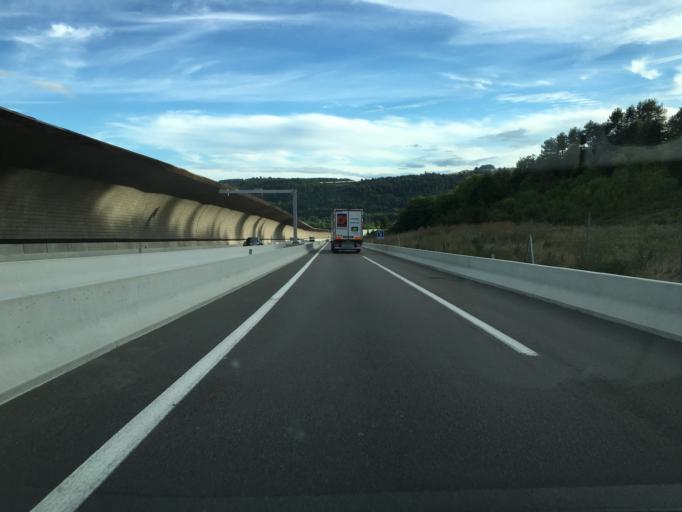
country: FR
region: Bourgogne
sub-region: Departement de la Cote-d'Or
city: Daix
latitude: 47.3411
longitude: 4.9866
